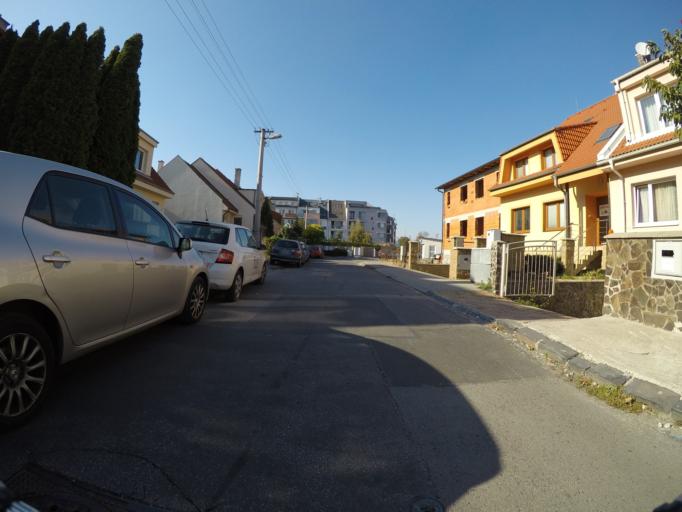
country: SK
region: Bratislavsky
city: Bratislava
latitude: 48.1679
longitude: 17.1655
